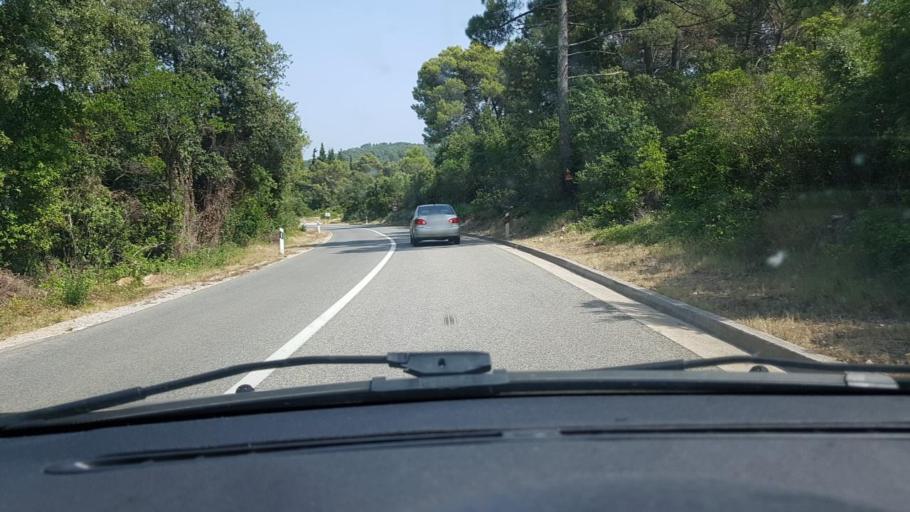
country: HR
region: Dubrovacko-Neretvanska
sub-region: Grad Korcula
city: Zrnovo
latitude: 42.9356
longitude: 17.1003
